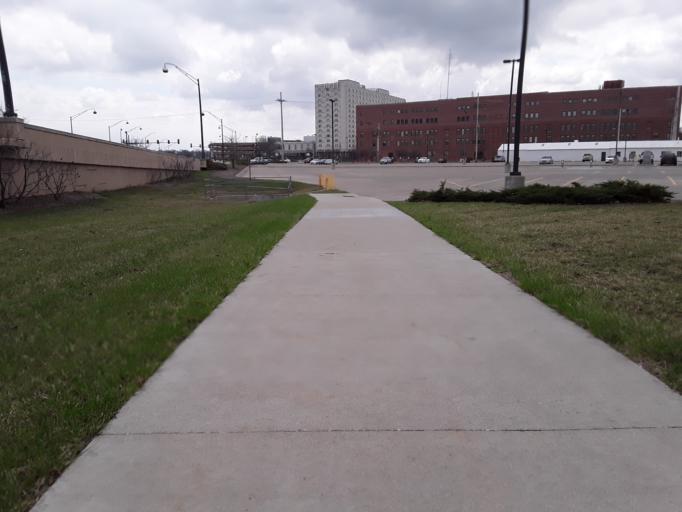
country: US
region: Nebraska
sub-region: Lancaster County
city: Lincoln
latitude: 40.8251
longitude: -96.6979
